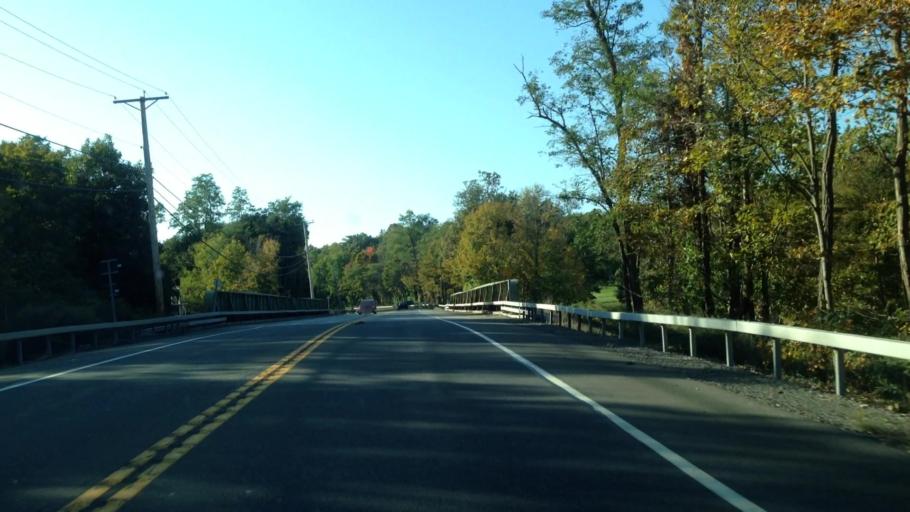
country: US
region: New York
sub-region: Dutchess County
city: Hyde Park
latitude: 41.7931
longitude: -73.9601
